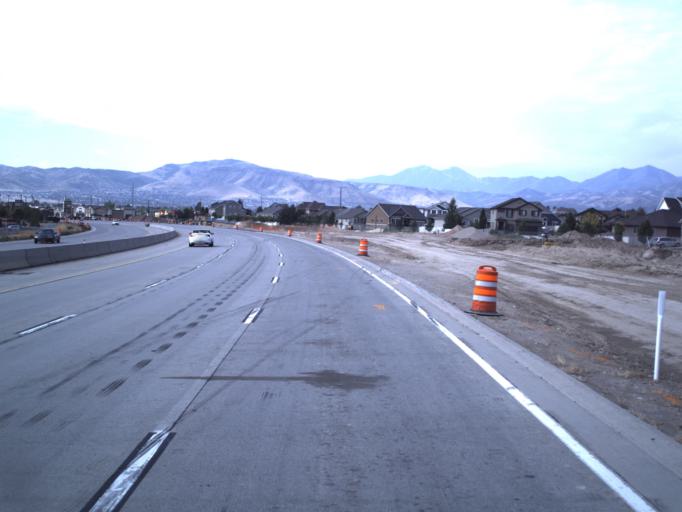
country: US
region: Utah
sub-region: Salt Lake County
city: South Jordan Heights
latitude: 40.5486
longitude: -111.9826
